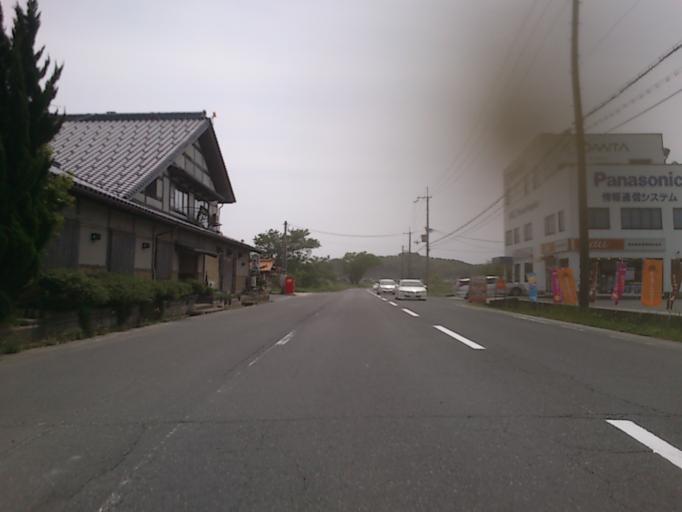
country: JP
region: Kyoto
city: Miyazu
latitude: 35.6686
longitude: 135.0866
